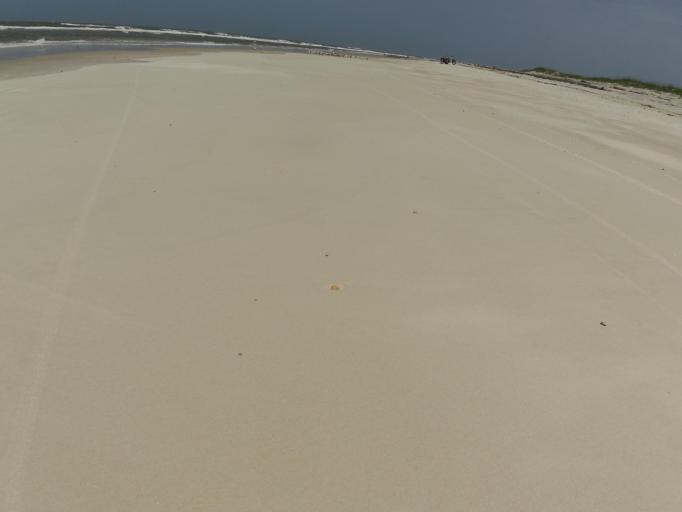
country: US
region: Florida
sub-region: Saint Johns County
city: Saint Augustine
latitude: 29.9081
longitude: -81.2836
